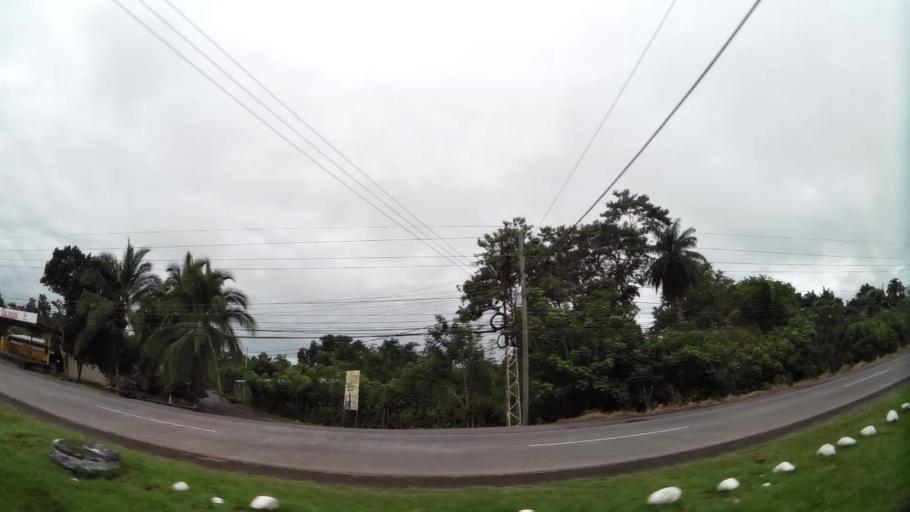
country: PA
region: Chiriqui
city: Boqueron
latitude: 8.4975
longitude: -82.5912
